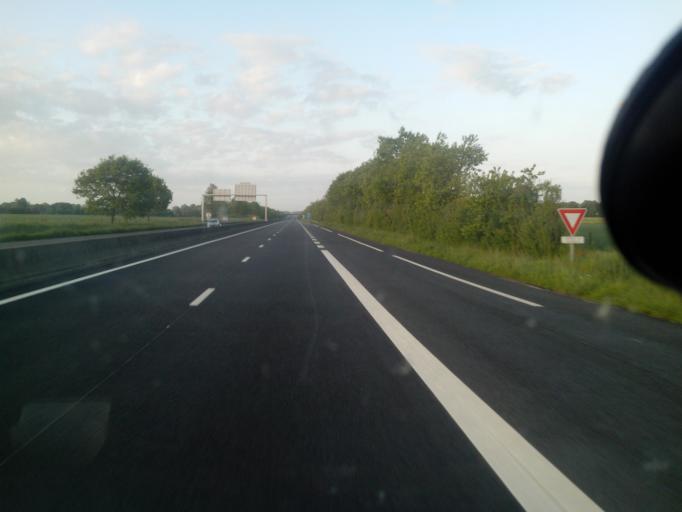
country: FR
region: Picardie
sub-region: Departement de la Somme
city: Oisemont
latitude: 50.0165
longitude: 1.7147
